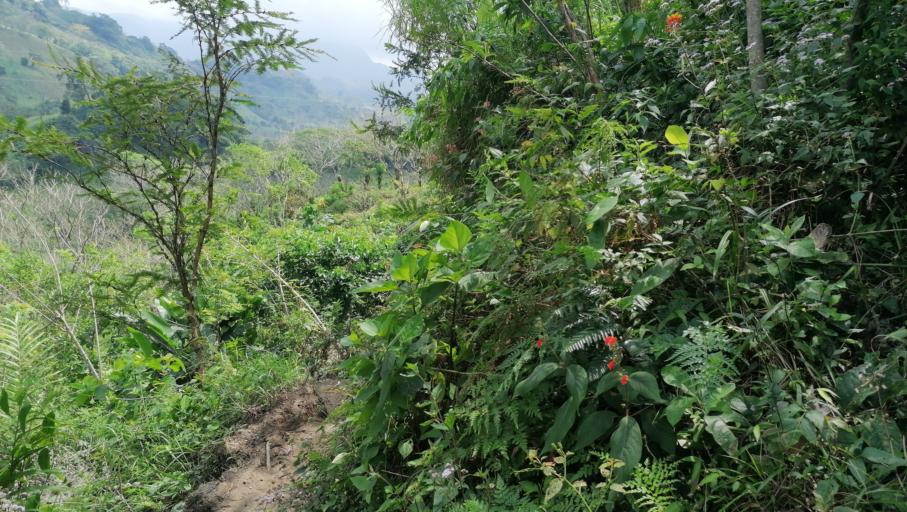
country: MX
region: Chiapas
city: Ocotepec
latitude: 17.2952
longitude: -93.2274
